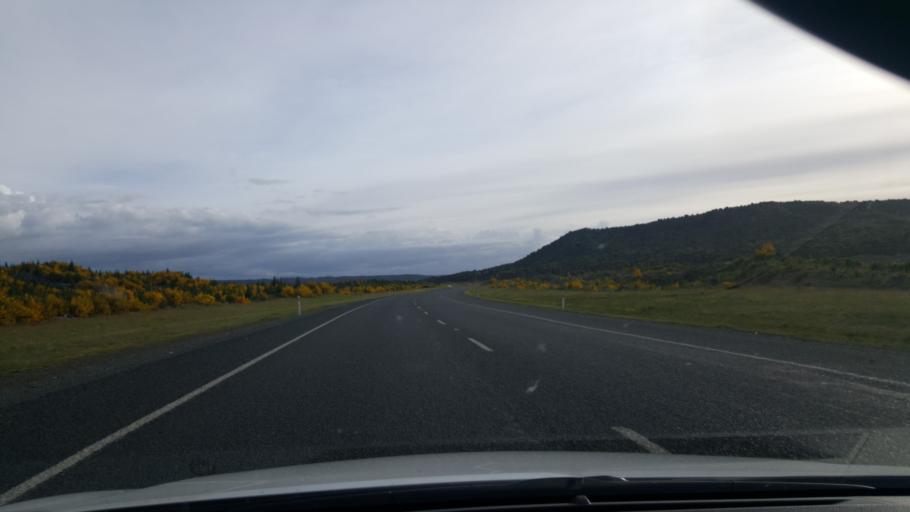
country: NZ
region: Waikato
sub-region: Taupo District
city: Taupo
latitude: -38.8394
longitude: 176.0635
